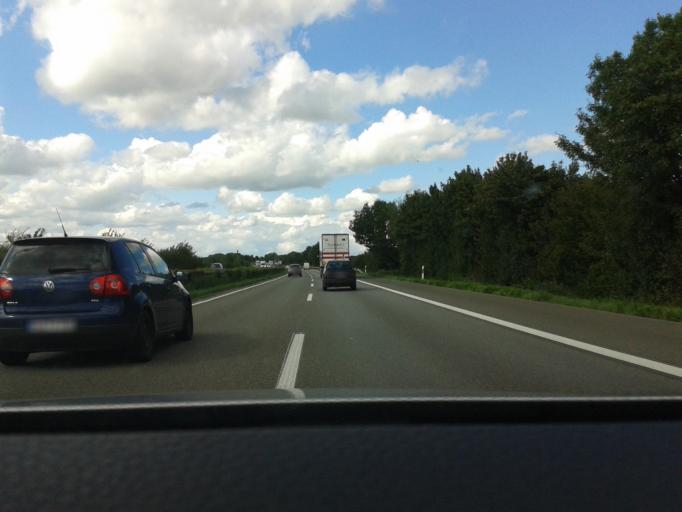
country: DE
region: North Rhine-Westphalia
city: Rheinberg
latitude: 51.5423
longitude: 6.5669
